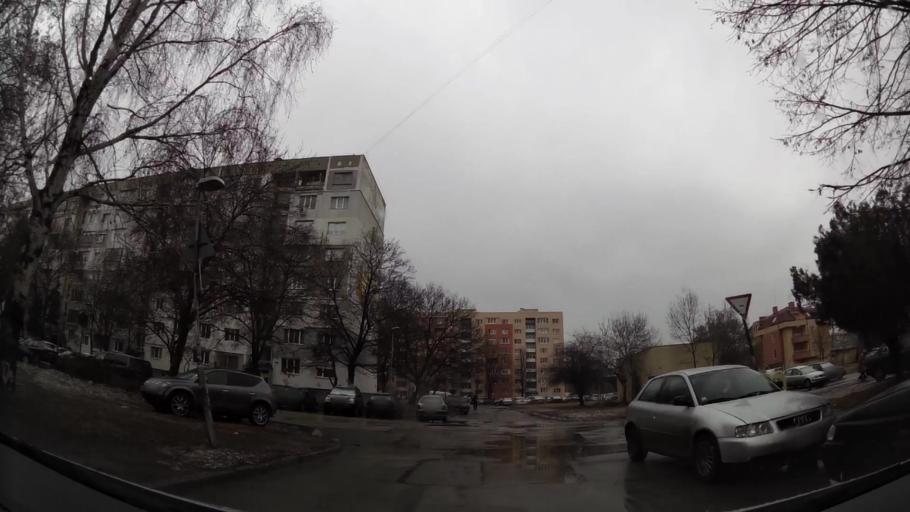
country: BG
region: Sofia-Capital
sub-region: Stolichna Obshtina
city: Sofia
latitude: 42.6703
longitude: 23.3912
